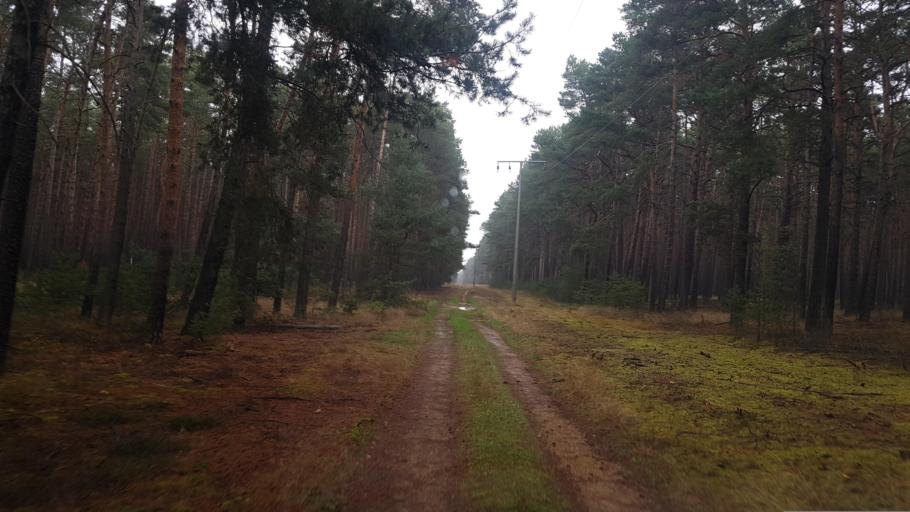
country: DE
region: Brandenburg
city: Crinitz
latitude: 51.6523
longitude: 13.7905
